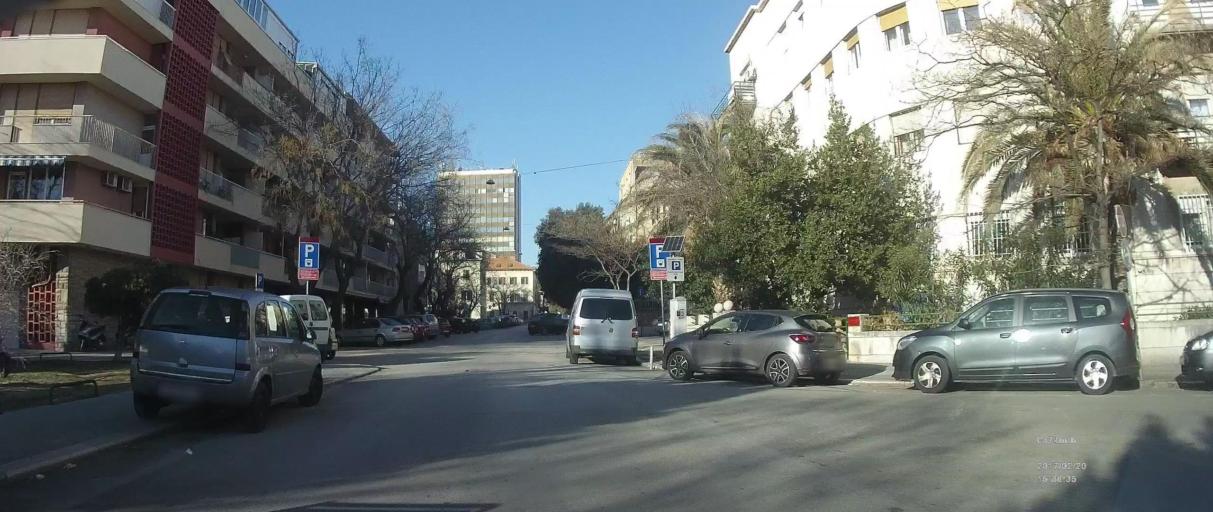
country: HR
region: Splitsko-Dalmatinska
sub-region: Grad Split
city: Split
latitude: 43.5038
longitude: 16.4454
